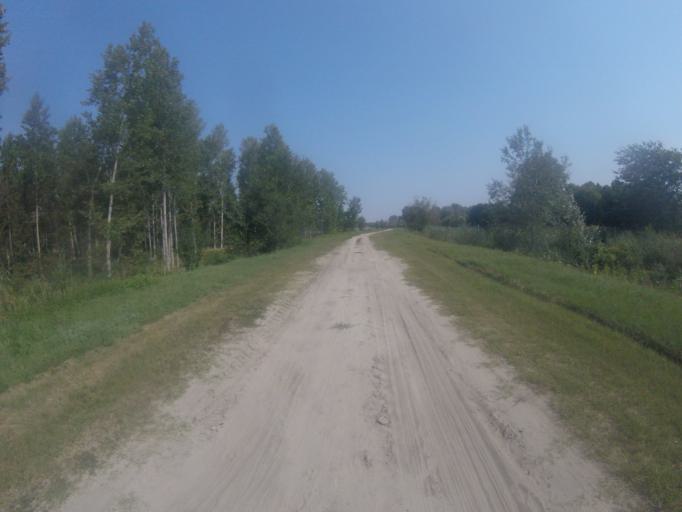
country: HU
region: Bacs-Kiskun
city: Ersekcsanad
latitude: 46.2493
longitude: 18.9691
